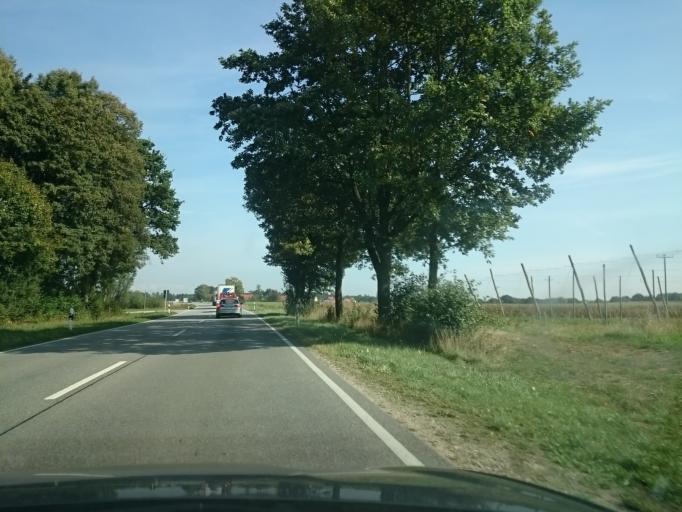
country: DE
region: Bavaria
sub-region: Upper Bavaria
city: Pornbach
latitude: 48.6051
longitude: 11.4283
